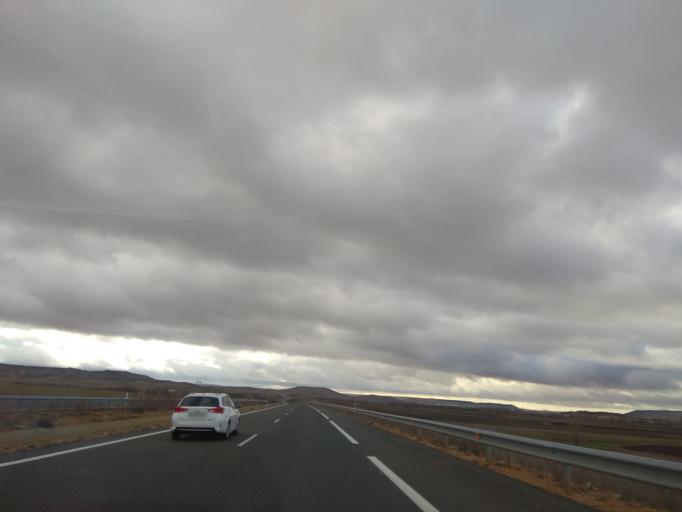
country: ES
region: Castille and Leon
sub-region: Provincia de Burgos
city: Quintanaortuno
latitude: 42.4326
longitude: -3.6944
